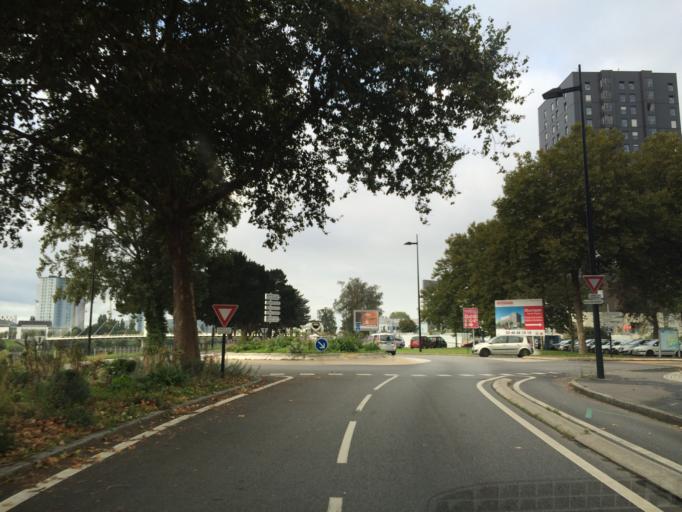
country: FR
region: Pays de la Loire
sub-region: Departement de la Loire-Atlantique
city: Saint-Sebastien-sur-Loire
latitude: 47.2147
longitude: -1.5248
